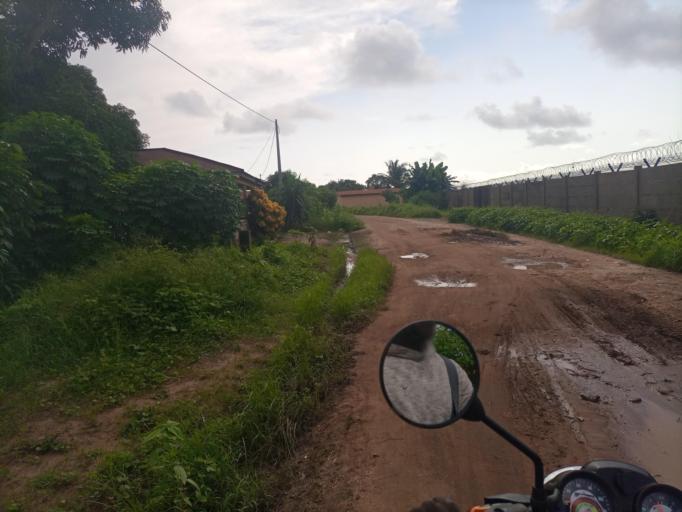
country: SL
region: Northern Province
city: Masoyila
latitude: 8.6108
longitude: -13.1839
